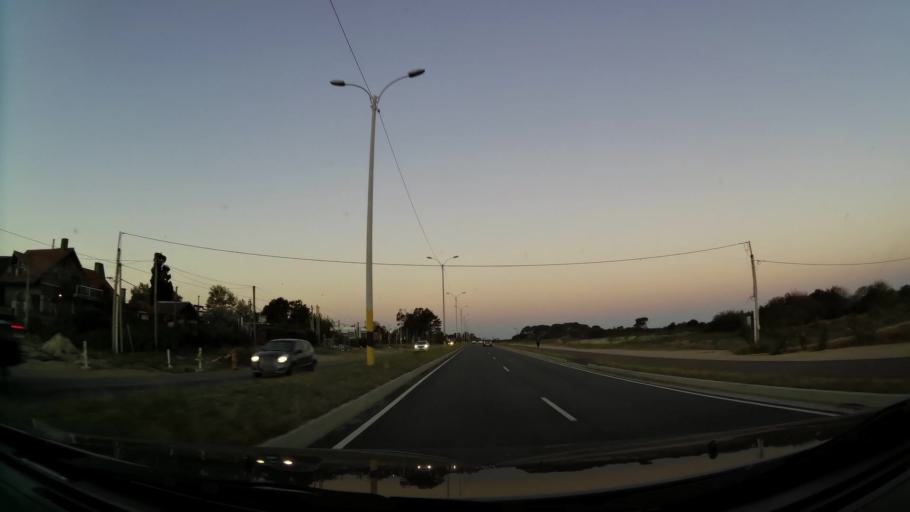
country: UY
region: Canelones
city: Barra de Carrasco
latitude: -34.8321
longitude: -55.9494
